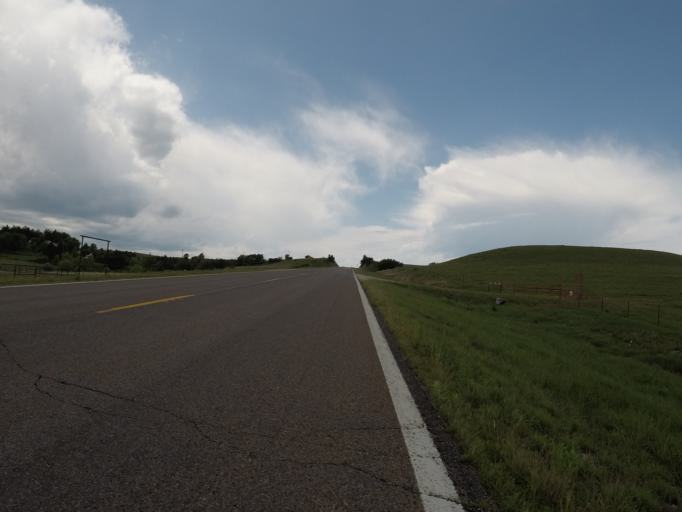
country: US
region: Kansas
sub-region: Wabaunsee County
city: Alma
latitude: 38.8709
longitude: -96.3580
